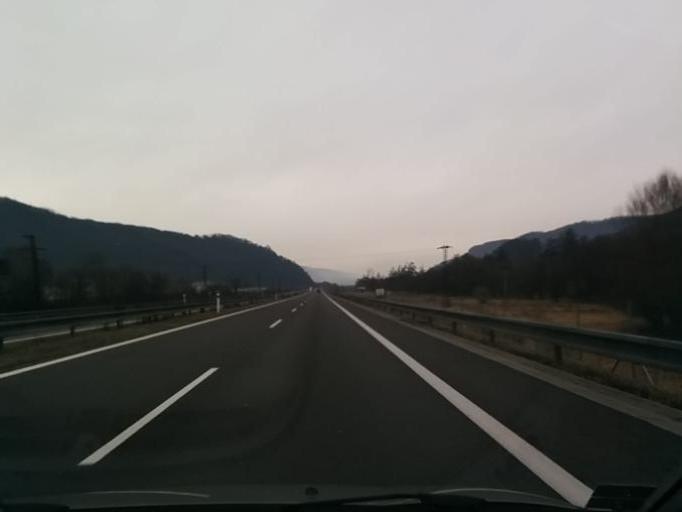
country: SK
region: Banskobystricky
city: Zarnovica
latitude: 48.4862
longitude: 18.7303
